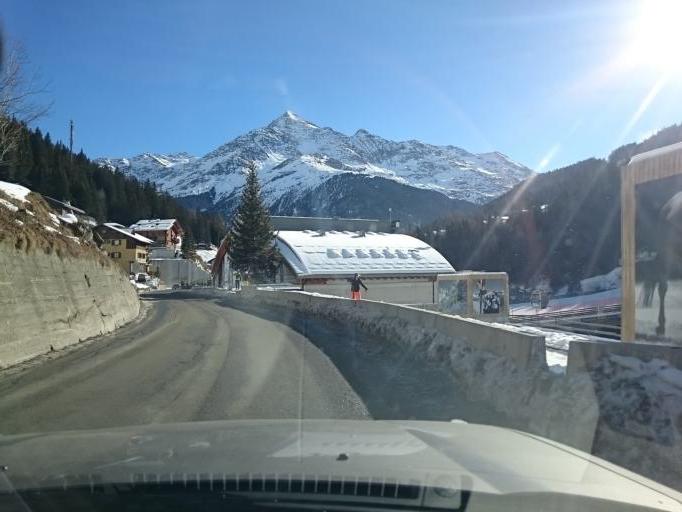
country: IT
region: Lombardy
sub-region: Provincia di Sondrio
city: Sant'Antonio
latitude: 46.4165
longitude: 10.4855
